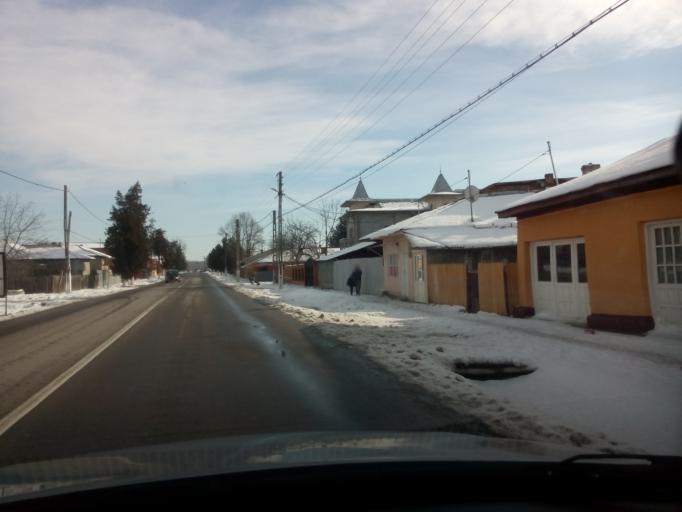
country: RO
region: Calarasi
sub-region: Comuna Budesti
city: Budesti
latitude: 44.2345
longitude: 26.4649
